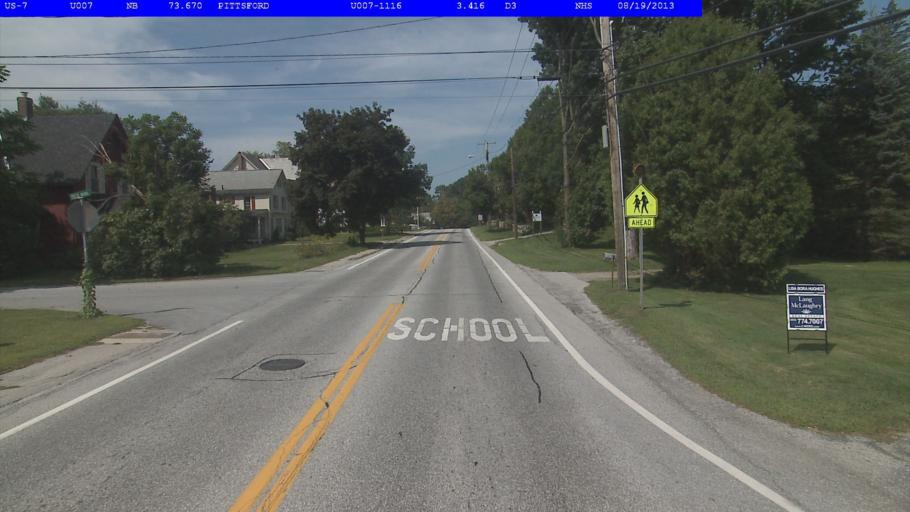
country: US
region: Vermont
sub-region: Rutland County
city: Rutland
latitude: 43.7065
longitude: -73.0171
